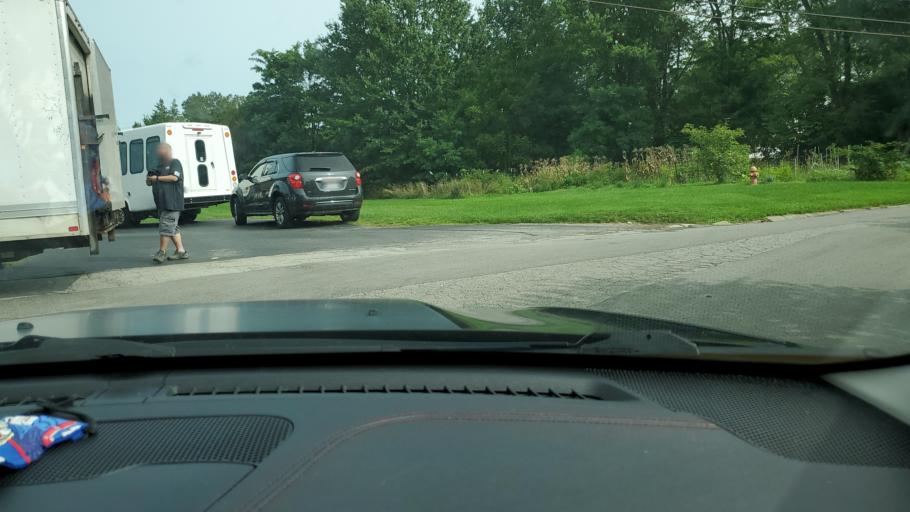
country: US
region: Ohio
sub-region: Mahoning County
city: Boardman
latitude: 41.0598
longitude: -80.6706
